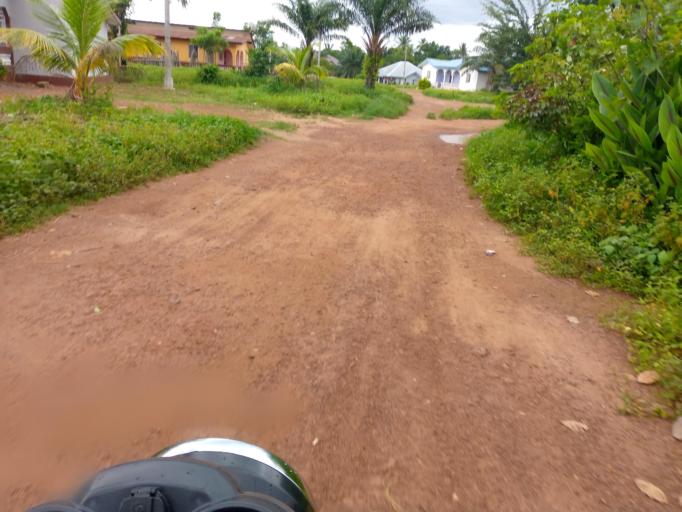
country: SL
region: Southern Province
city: Moyamba
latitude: 8.1531
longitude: -12.4355
